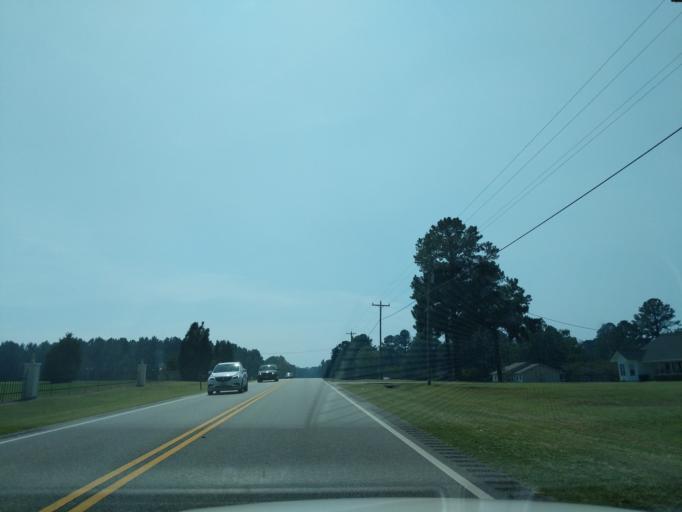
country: US
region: Alabama
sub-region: Covington County
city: Andalusia
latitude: 31.2616
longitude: -86.5152
